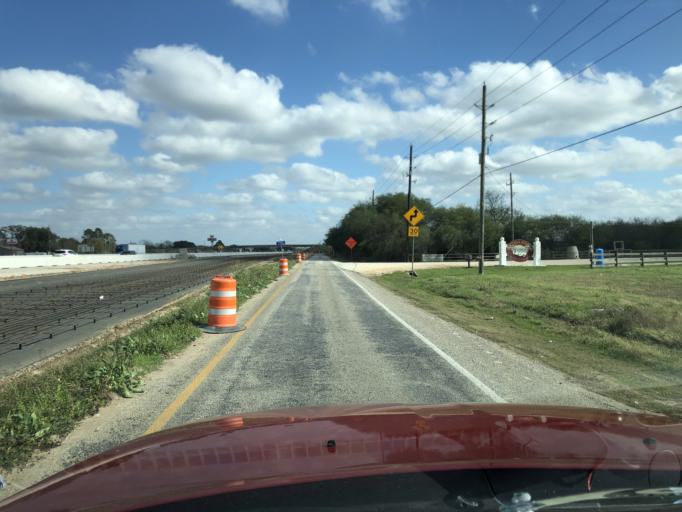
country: US
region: Texas
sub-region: Austin County
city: Sealy
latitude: 29.7756
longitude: -96.1142
